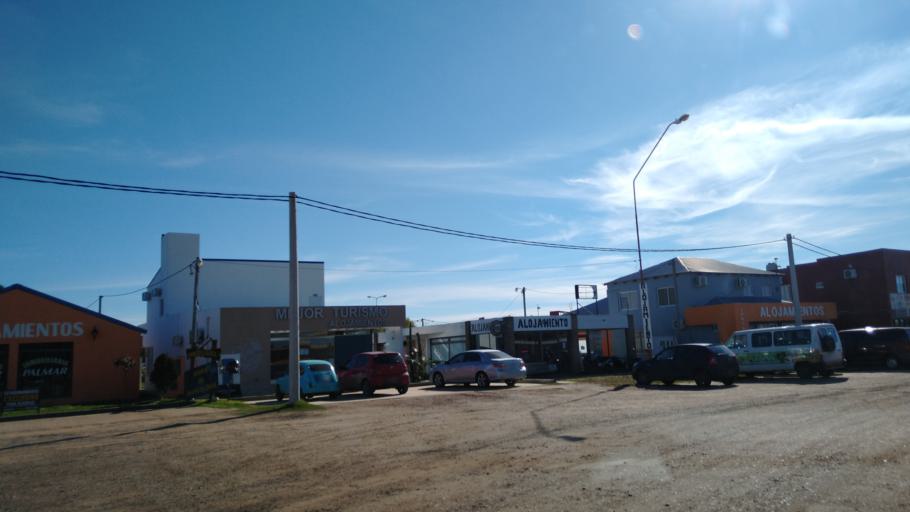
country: AR
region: Entre Rios
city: Chajari
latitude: -30.7454
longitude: -58.0117
